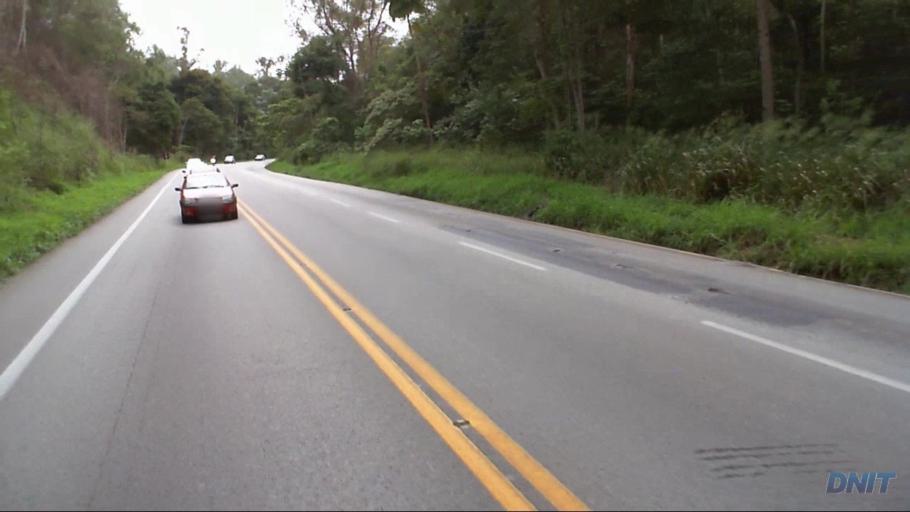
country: BR
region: Minas Gerais
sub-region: Joao Monlevade
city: Joao Monlevade
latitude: -19.8466
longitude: -43.1084
